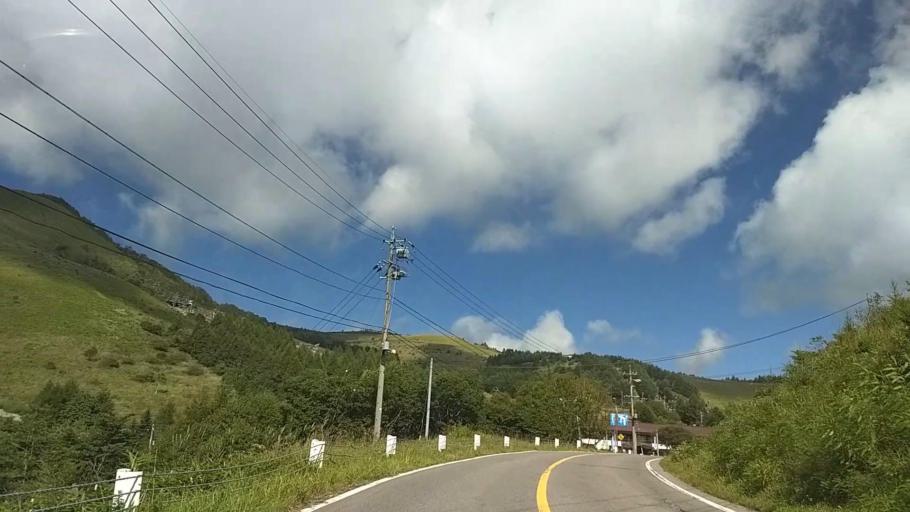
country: JP
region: Nagano
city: Suwa
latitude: 36.1000
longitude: 138.2137
